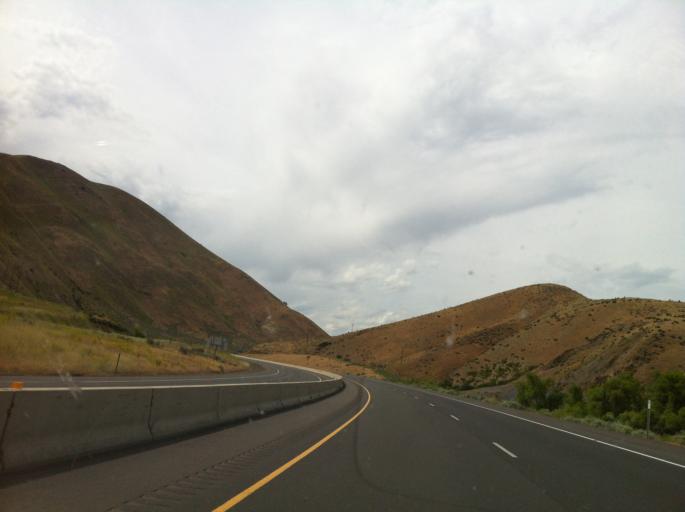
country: US
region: Idaho
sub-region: Washington County
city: Weiser
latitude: 44.4040
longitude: -117.3114
